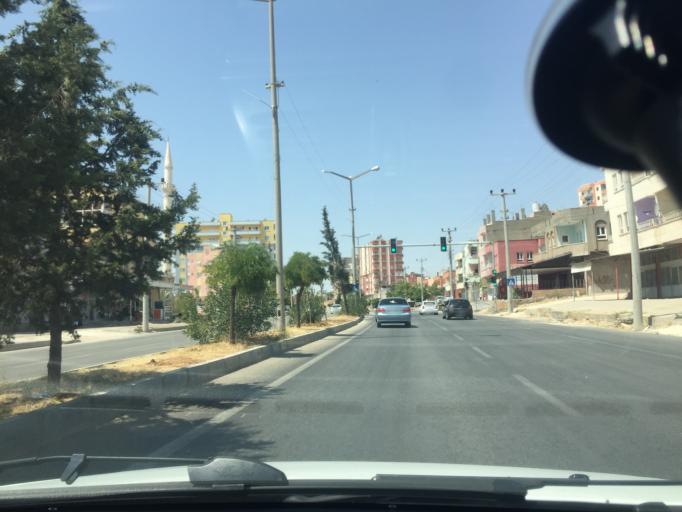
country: TR
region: Mardin
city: Midyat
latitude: 37.4289
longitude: 41.3440
